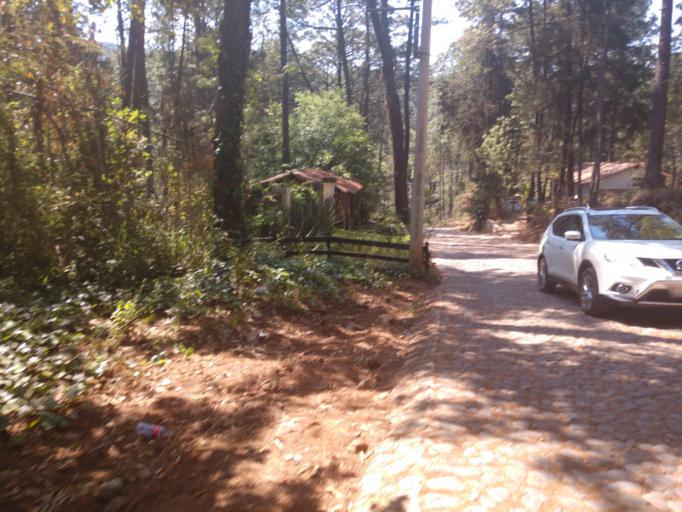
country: MX
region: Jalisco
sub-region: Mazamitla
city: Mazamitla
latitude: 19.9029
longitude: -103.0321
